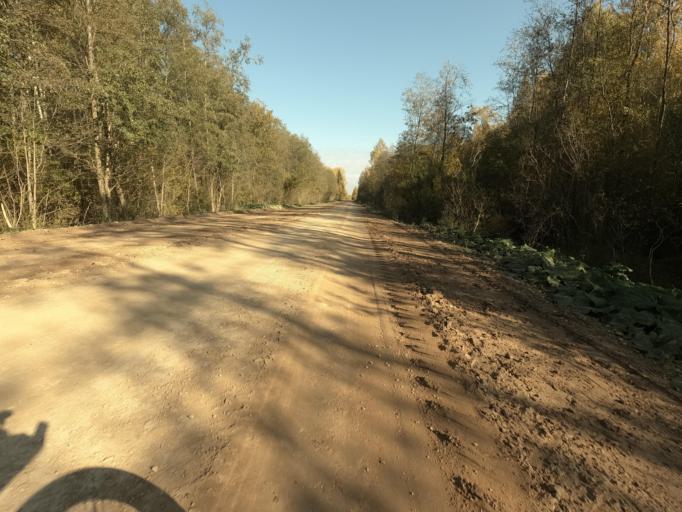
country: RU
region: Novgorod
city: Batetskiy
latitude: 58.8268
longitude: 30.7101
